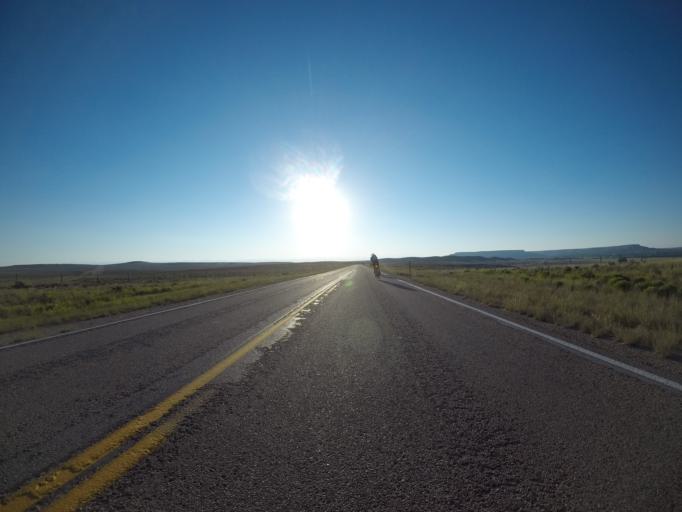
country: US
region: Wyoming
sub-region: Sublette County
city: Marbleton
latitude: 42.5799
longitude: -109.9992
